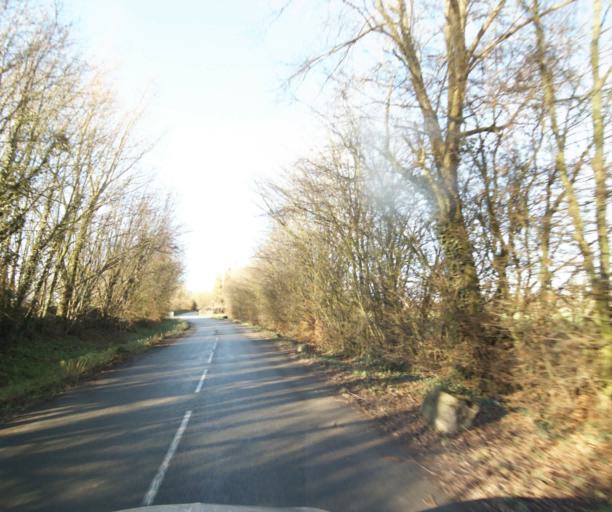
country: FR
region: Nord-Pas-de-Calais
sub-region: Departement du Nord
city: Curgies
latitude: 50.3235
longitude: 3.5998
